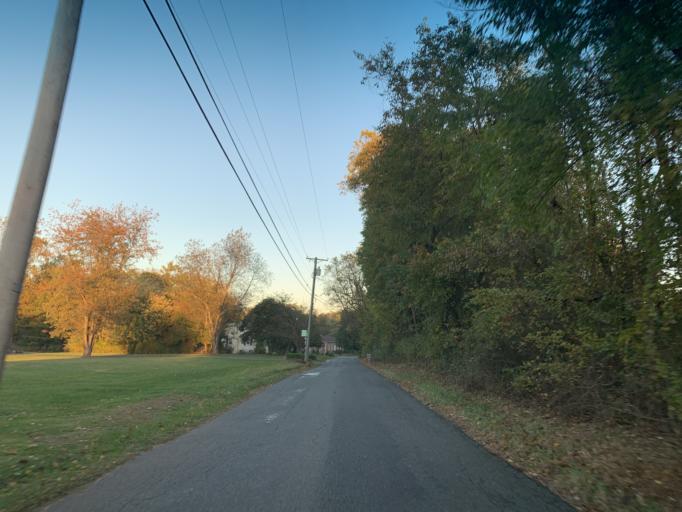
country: US
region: Maryland
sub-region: Baltimore County
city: Kingsville
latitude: 39.4697
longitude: -76.4218
